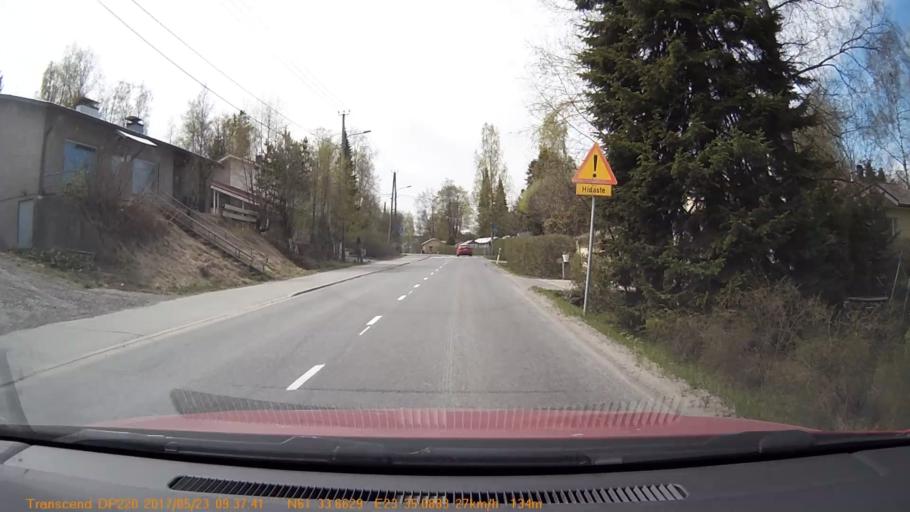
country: FI
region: Pirkanmaa
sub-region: Tampere
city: Yloejaervi
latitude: 61.5610
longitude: 23.5848
